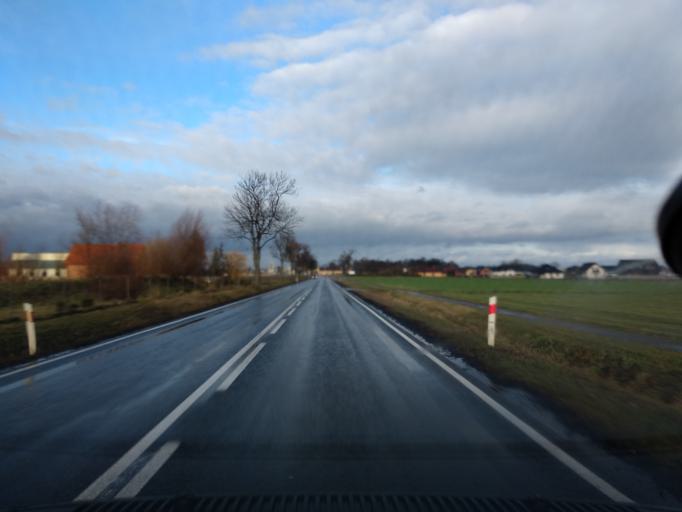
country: PL
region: Greater Poland Voivodeship
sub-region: Powiat koninski
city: Rychwal
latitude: 52.0607
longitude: 18.1637
